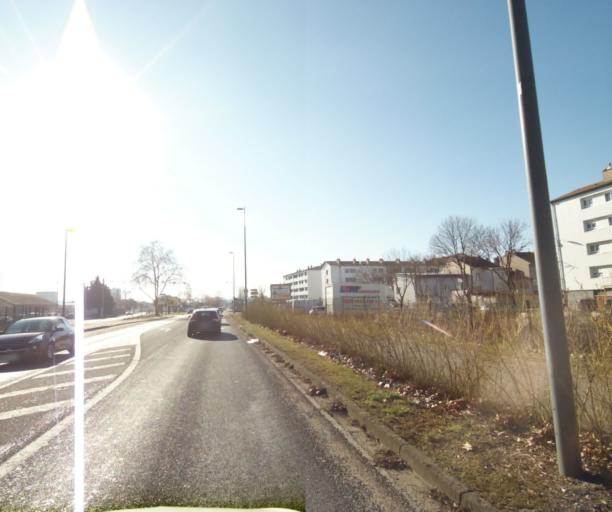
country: FR
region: Lorraine
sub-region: Departement de Meurthe-et-Moselle
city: Essey-les-Nancy
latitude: 48.7043
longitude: 6.2321
